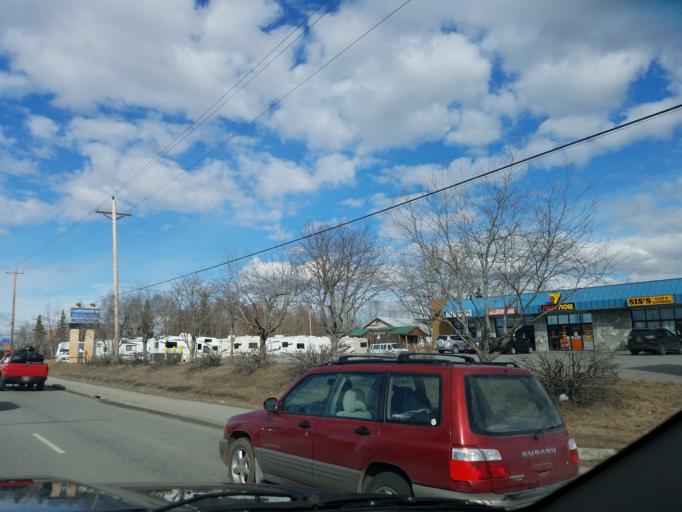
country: US
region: Alaska
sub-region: Anchorage Municipality
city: Anchorage
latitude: 61.1711
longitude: -149.8681
